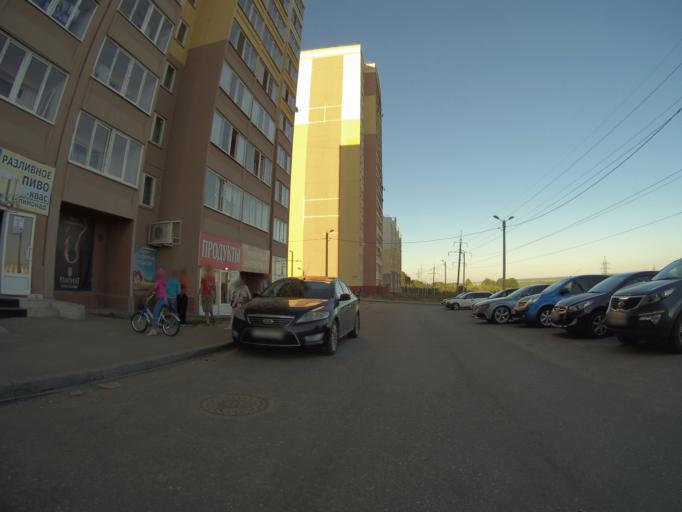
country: RU
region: Vladimir
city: Vladimir
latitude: 56.1049
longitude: 40.3659
